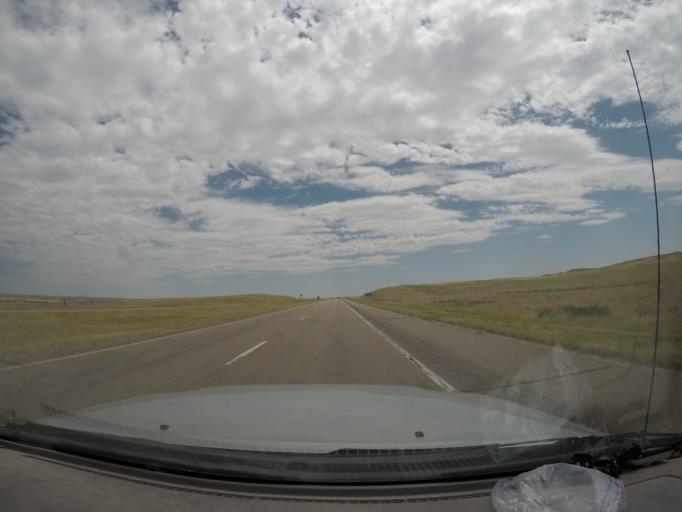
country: US
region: Nebraska
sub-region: Cheyenne County
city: Sidney
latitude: 41.1748
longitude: -103.1204
